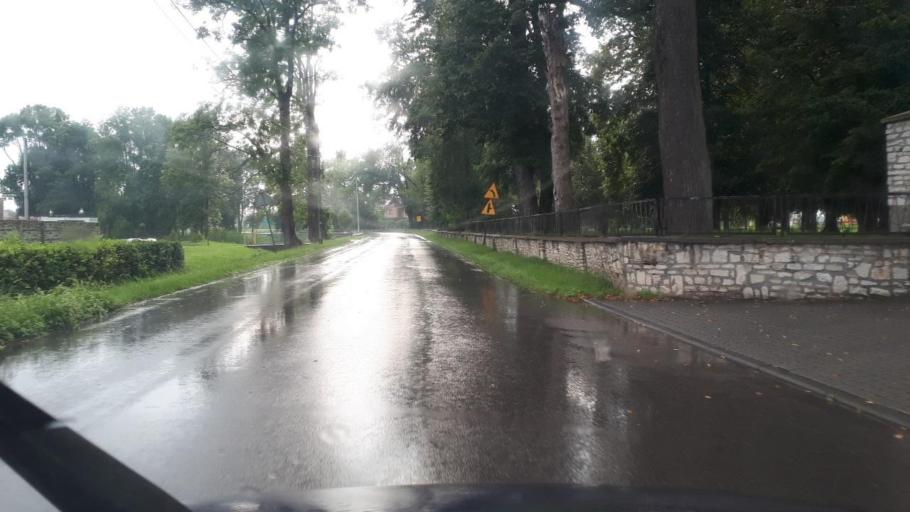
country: PL
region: Silesian Voivodeship
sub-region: Powiat gliwicki
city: Wielowies
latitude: 50.5053
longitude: 18.6079
